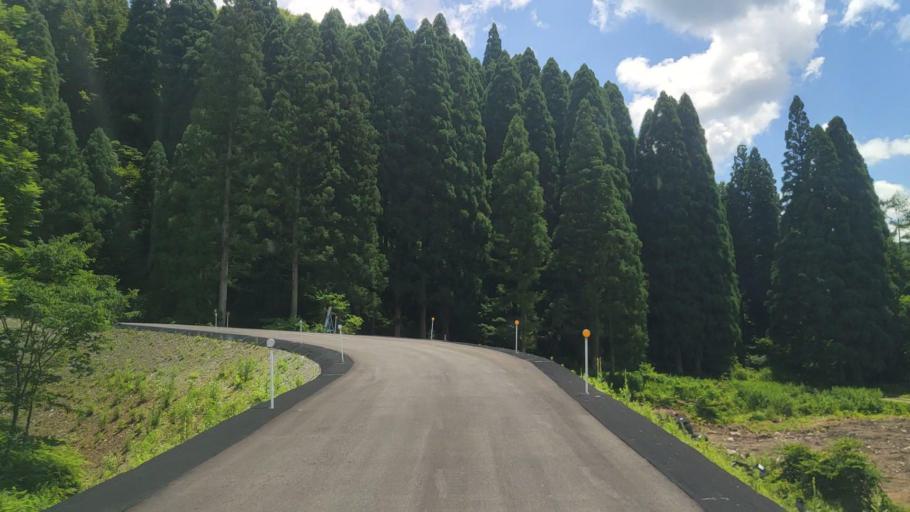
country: JP
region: Fukui
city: Ono
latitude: 35.8191
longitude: 136.4522
